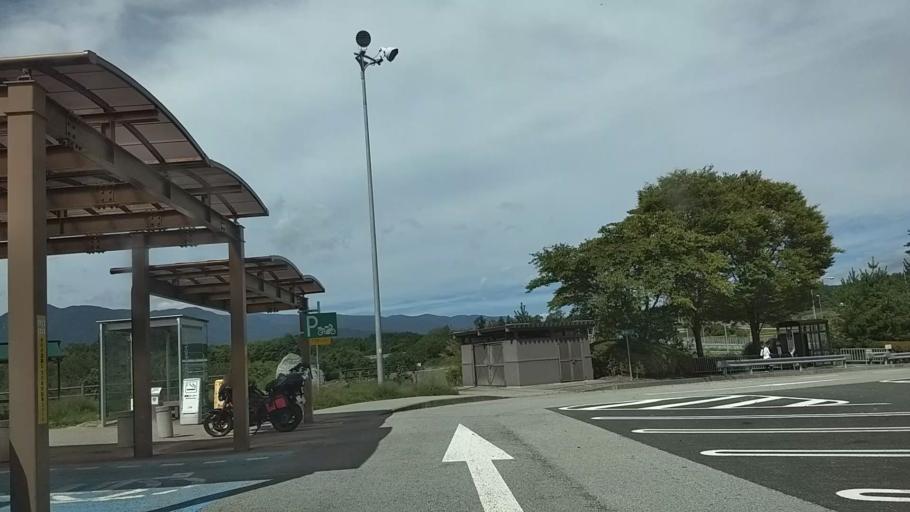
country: JP
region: Yamanashi
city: Nirasaki
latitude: 35.8440
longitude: 138.3681
